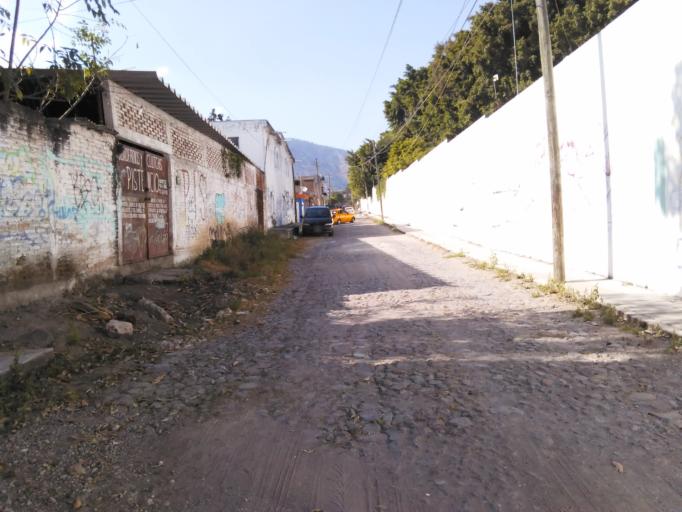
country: MX
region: Nayarit
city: Tepic
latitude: 21.4898
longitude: -104.8962
